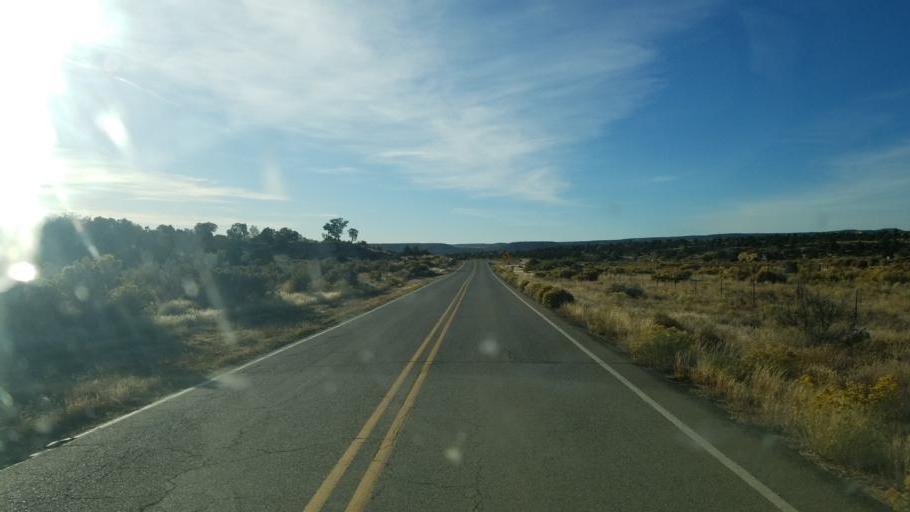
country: US
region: New Mexico
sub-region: San Juan County
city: Bloomfield
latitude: 36.7337
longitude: -107.7758
